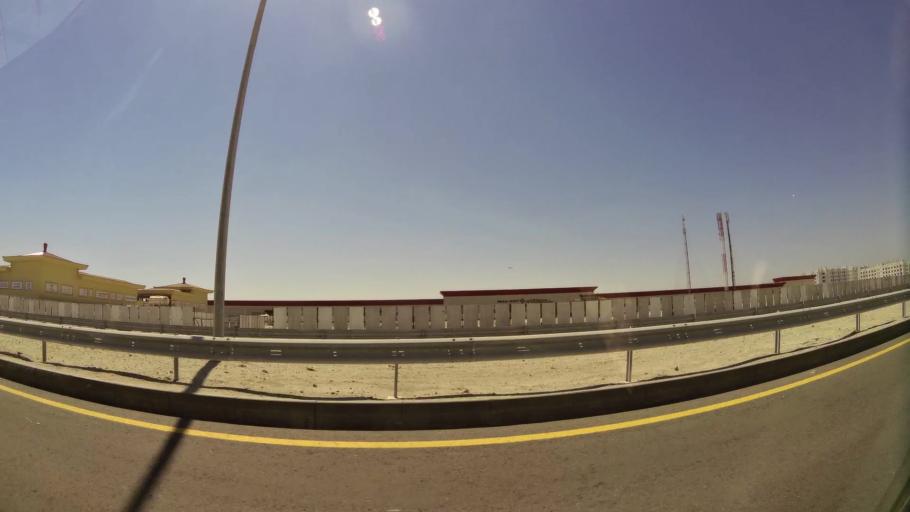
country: BH
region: Muharraq
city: Al Muharraq
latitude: 26.3076
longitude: 50.6268
